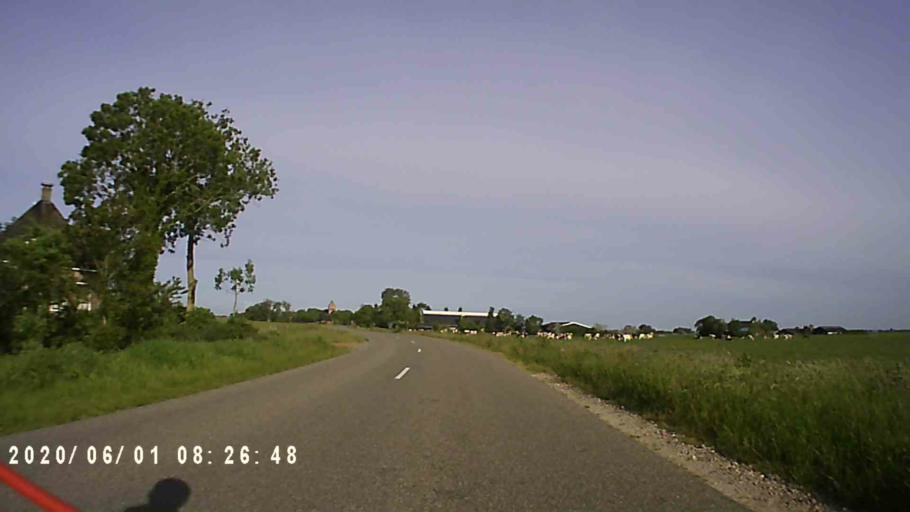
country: NL
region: Friesland
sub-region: Gemeente Ferwerderadiel
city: Burdaard
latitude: 53.2996
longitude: 5.8597
